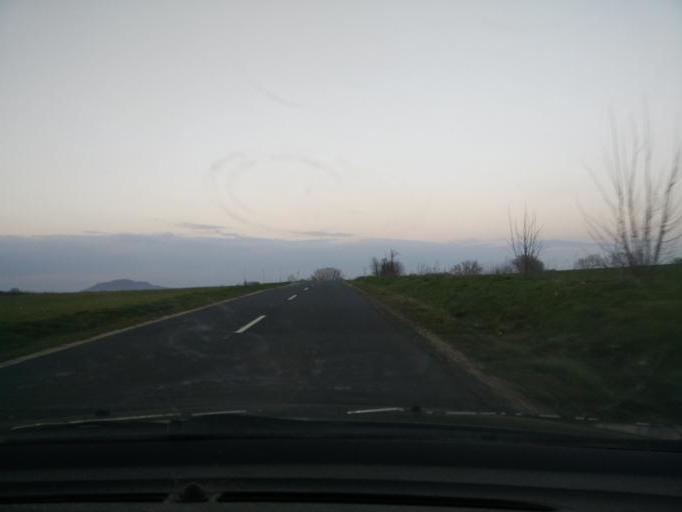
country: HU
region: Veszprem
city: Csabrendek
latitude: 47.0479
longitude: 17.3314
